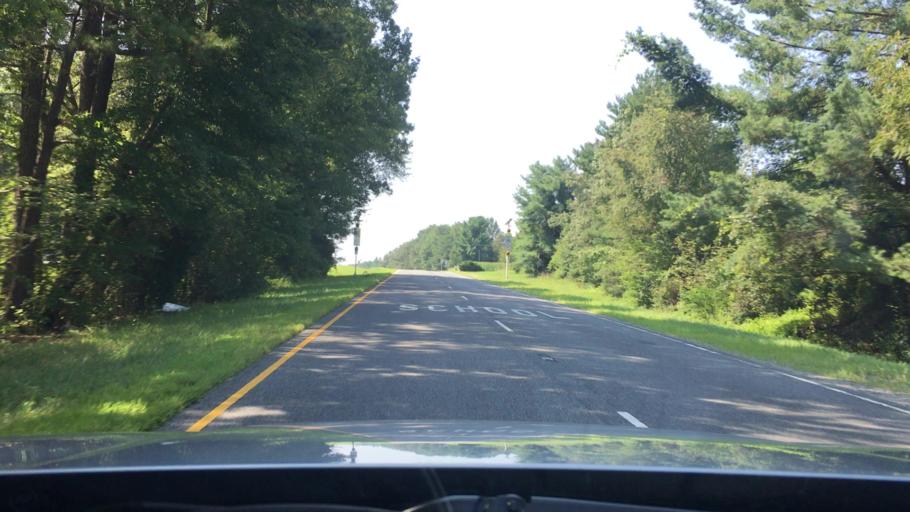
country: US
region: Virginia
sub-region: Caroline County
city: Bowling Green
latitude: 38.0044
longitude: -77.4150
